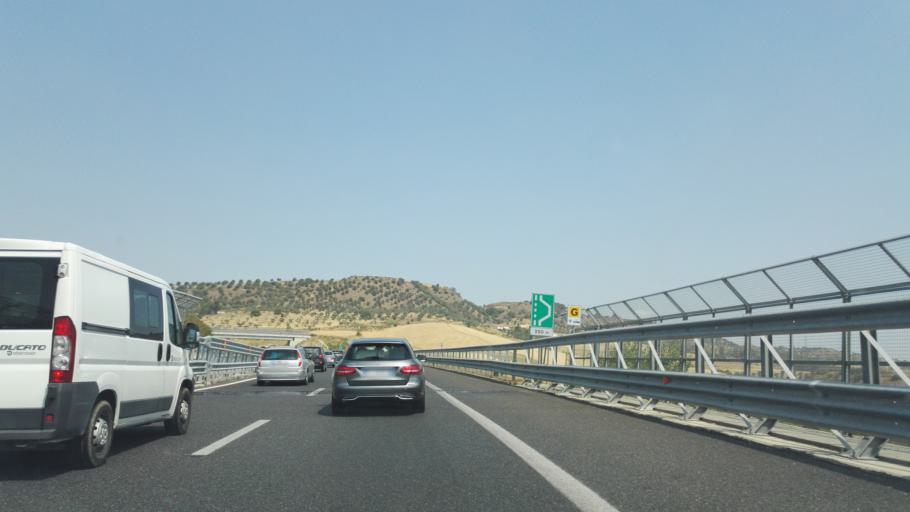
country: IT
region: Calabria
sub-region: Provincia di Cosenza
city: Tarsia
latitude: 39.5940
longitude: 16.2454
